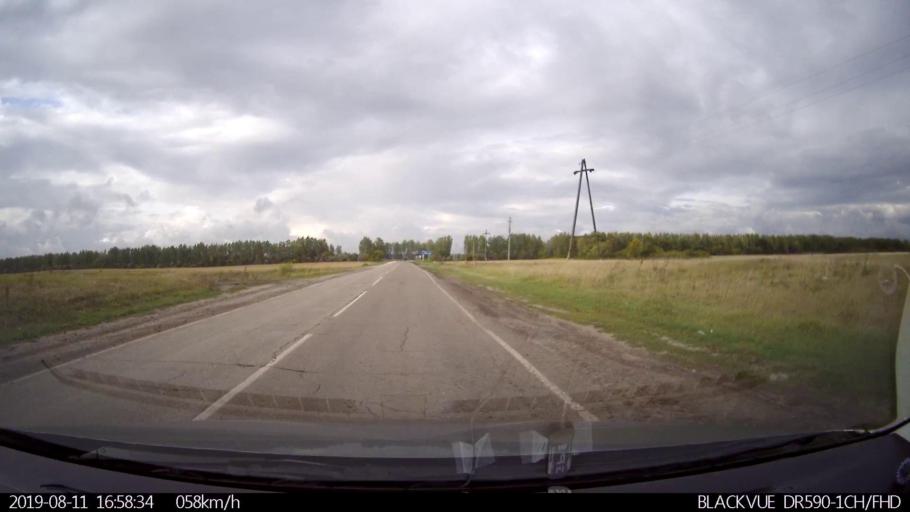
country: RU
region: Ulyanovsk
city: Mayna
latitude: 54.3093
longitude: 47.6564
